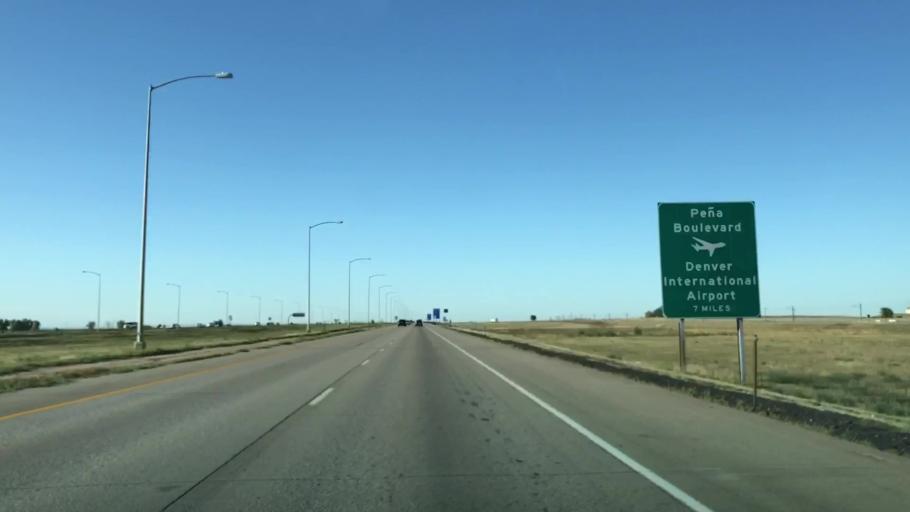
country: US
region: Colorado
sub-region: Adams County
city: Aurora
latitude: 39.8098
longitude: -104.7859
